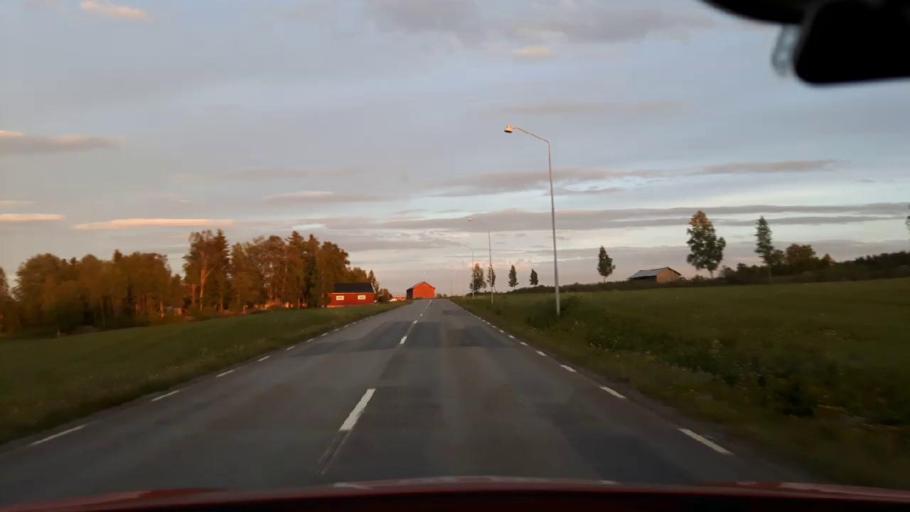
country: SE
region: Jaemtland
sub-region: OEstersunds Kommun
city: Brunflo
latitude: 63.1033
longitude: 14.7376
